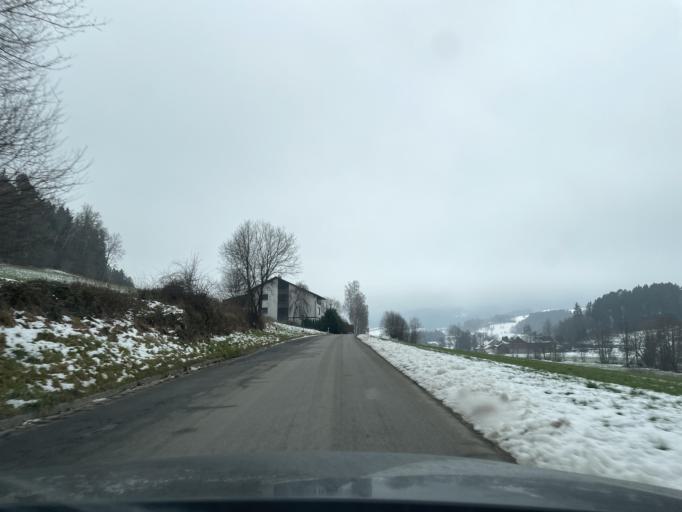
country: DE
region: Bavaria
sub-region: Lower Bavaria
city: Kollnburg
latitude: 49.0353
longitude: 12.8841
